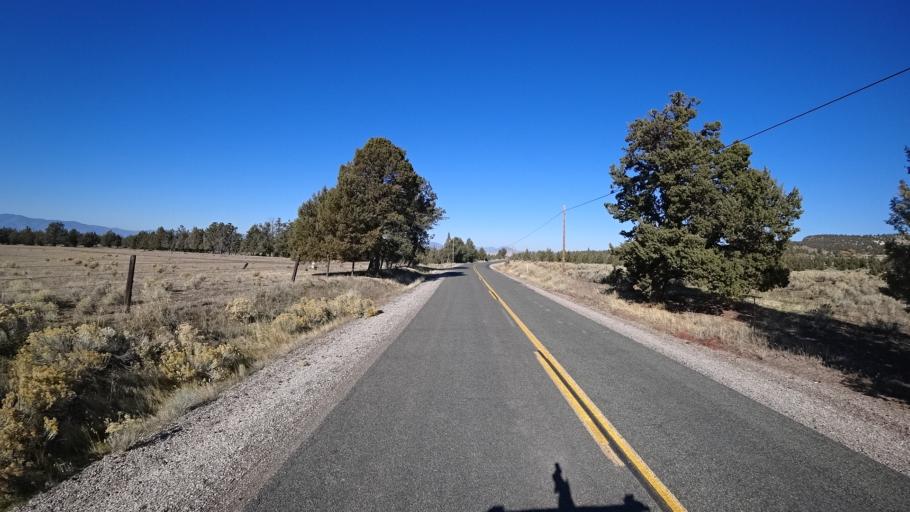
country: US
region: California
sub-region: Siskiyou County
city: Montague
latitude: 41.6352
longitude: -122.3385
